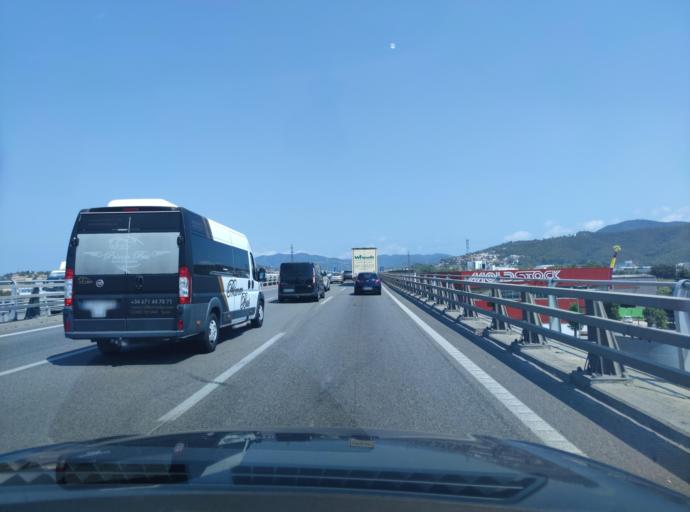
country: ES
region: Catalonia
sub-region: Provincia de Barcelona
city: Montmelo
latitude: 41.5495
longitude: 2.2281
